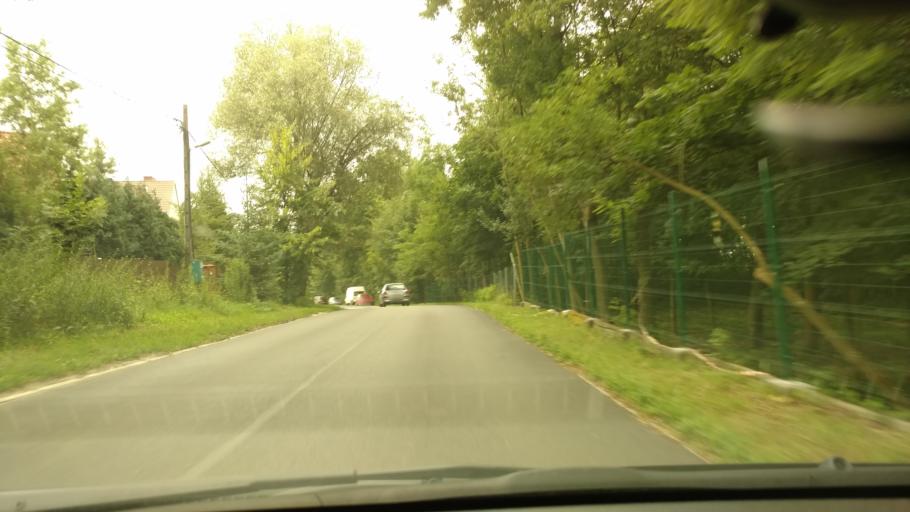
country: PL
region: Lesser Poland Voivodeship
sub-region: Powiat krakowski
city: Zielonki
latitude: 50.1110
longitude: 19.9430
